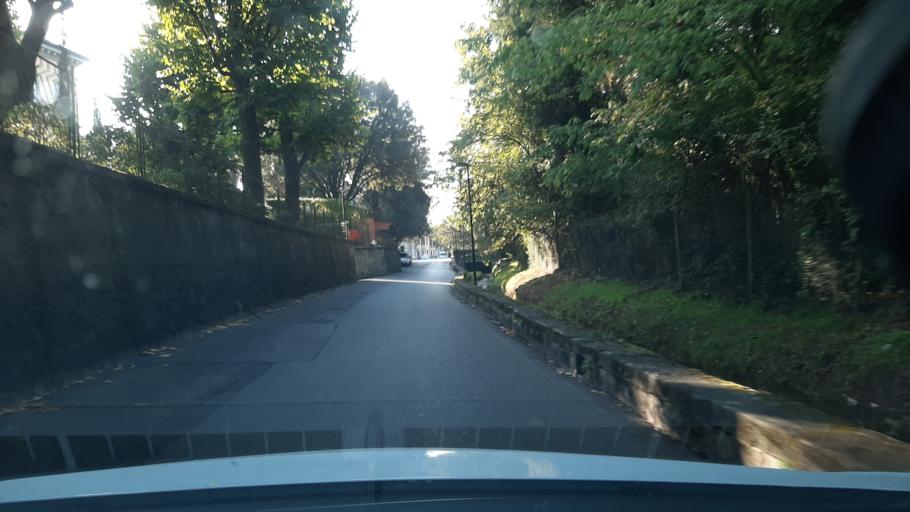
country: IT
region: Tuscany
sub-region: Province of Florence
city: Fiesole
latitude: 43.7869
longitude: 11.2941
